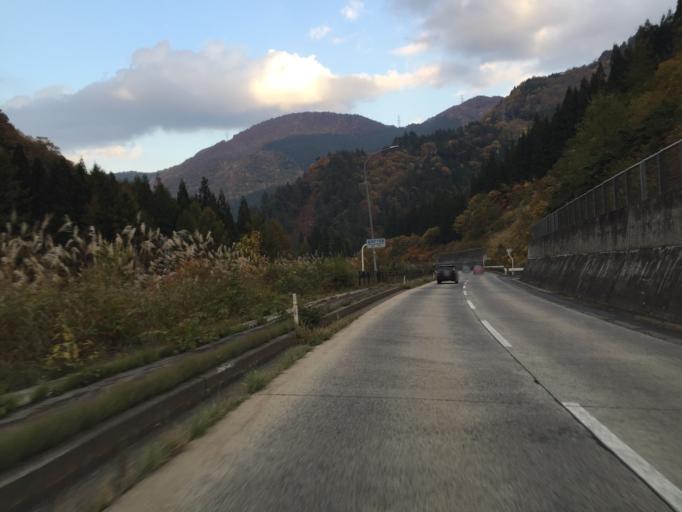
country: JP
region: Yamagata
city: Yonezawa
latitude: 37.8110
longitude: 139.9929
